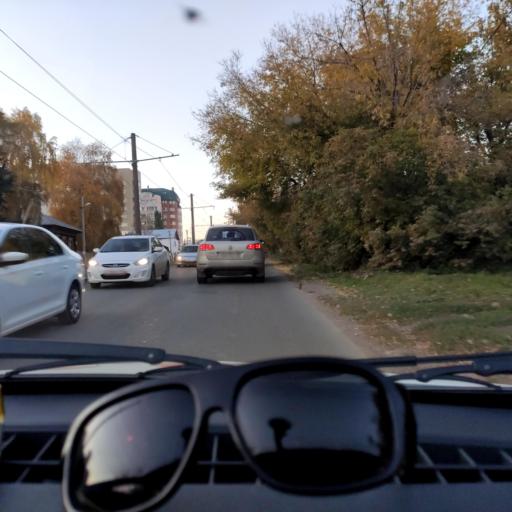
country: RU
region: Bashkortostan
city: Ufa
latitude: 54.7208
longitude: 55.9677
